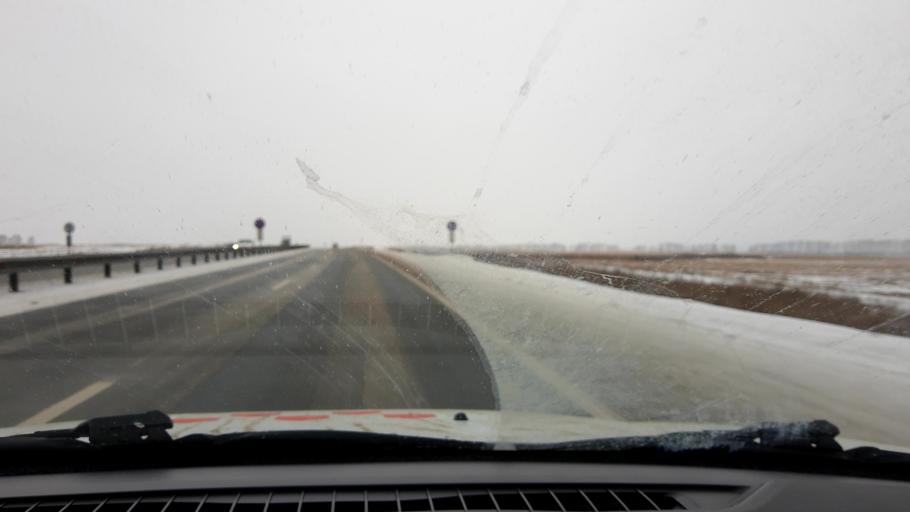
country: RU
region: Nizjnij Novgorod
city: Burevestnik
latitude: 56.1173
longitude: 43.9515
